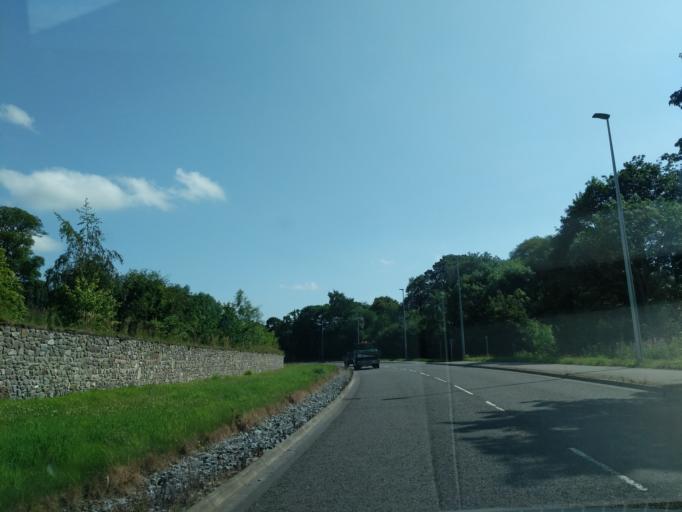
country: GB
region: Scotland
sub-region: Moray
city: Fochabers
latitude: 57.6175
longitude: -3.1039
